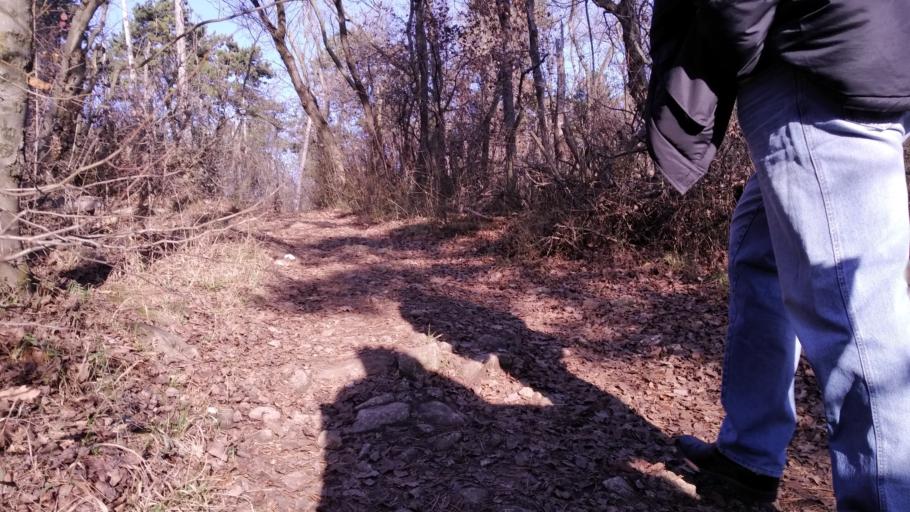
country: HU
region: Pest
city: Urom
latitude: 47.5515
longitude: 18.9907
